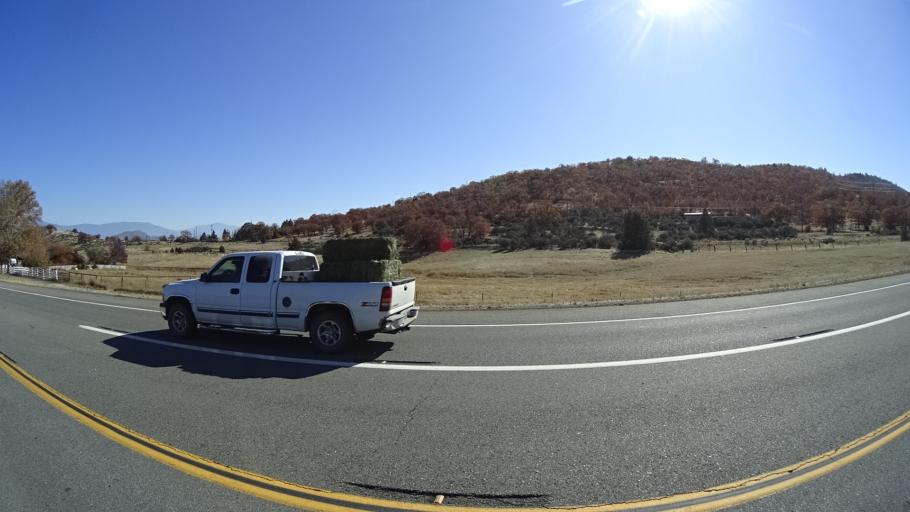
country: US
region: California
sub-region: Siskiyou County
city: Yreka
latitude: 41.7404
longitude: -122.6117
